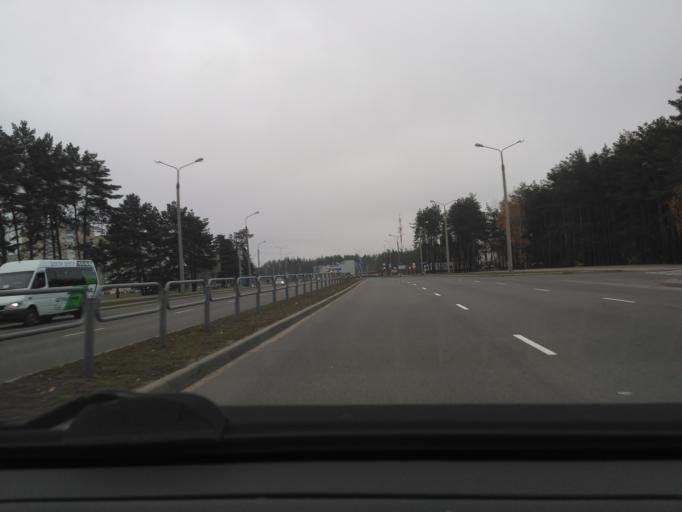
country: BY
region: Minsk
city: Horad Barysaw
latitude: 54.2014
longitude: 28.4796
